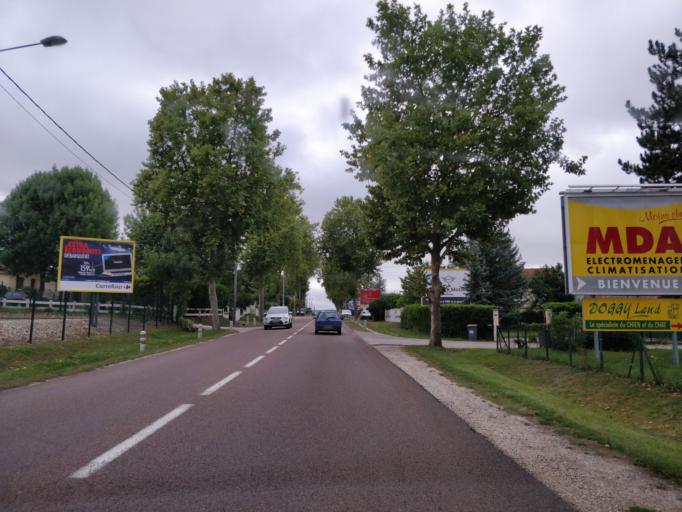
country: FR
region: Champagne-Ardenne
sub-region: Departement de l'Aube
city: Saint-Germain
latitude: 48.2675
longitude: 4.0459
